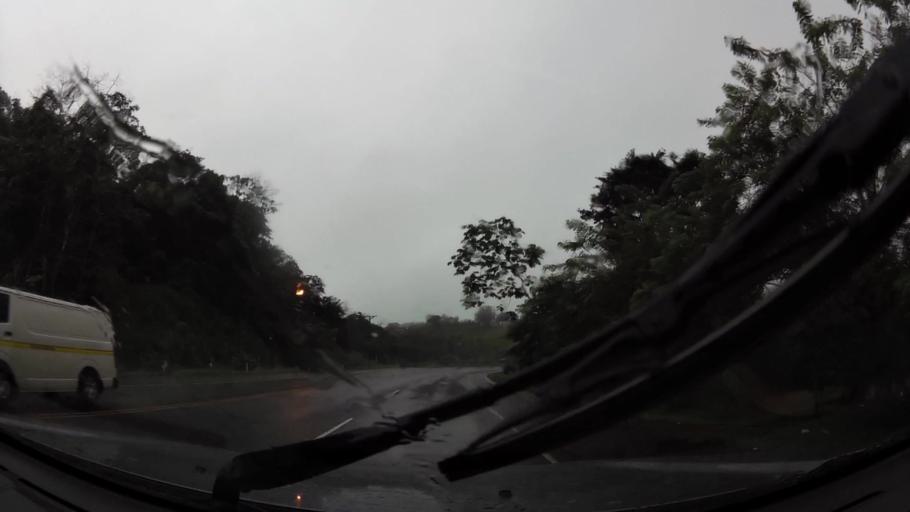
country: PA
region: Colon
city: Rio Rita
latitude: 9.3075
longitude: -79.7888
